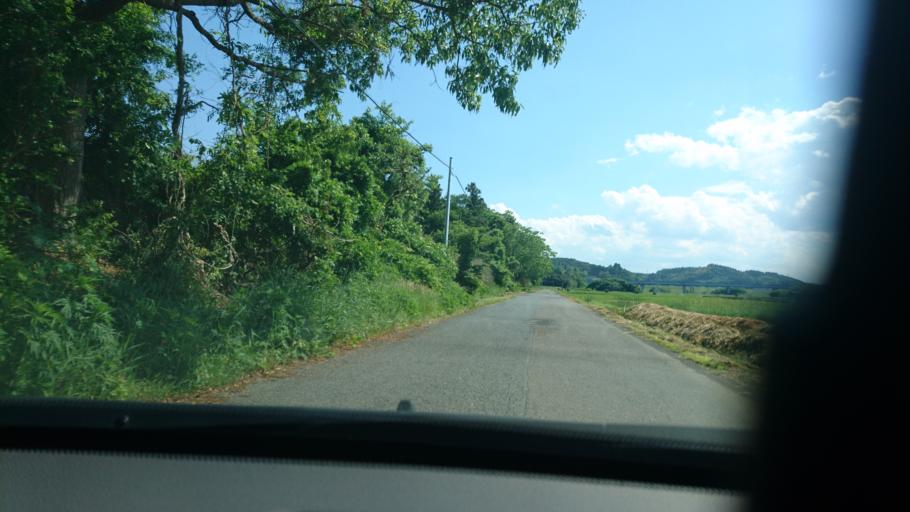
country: JP
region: Iwate
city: Ichinoseki
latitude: 38.9404
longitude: 141.1662
